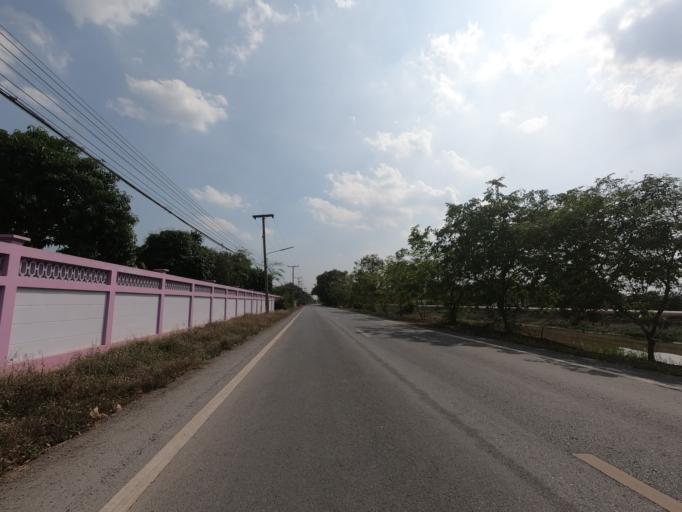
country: TH
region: Pathum Thani
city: Nong Suea
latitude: 14.1519
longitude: 100.8464
